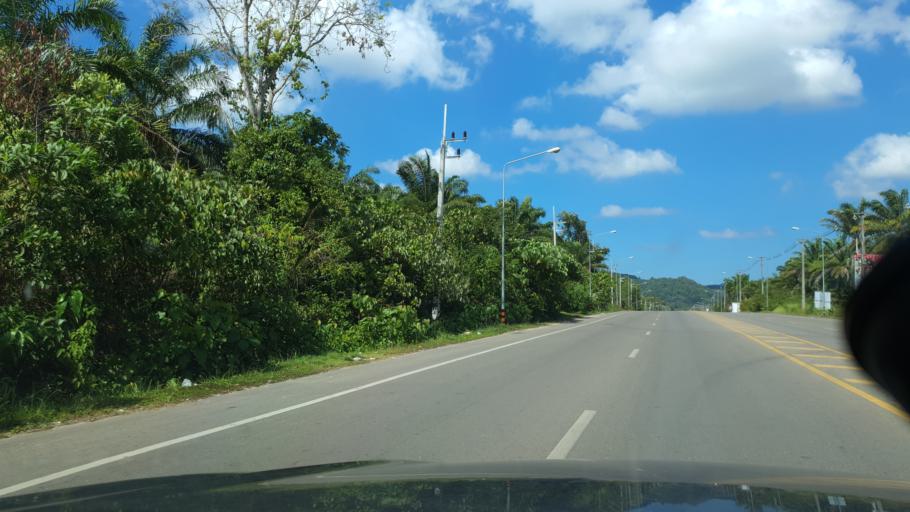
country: TH
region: Phangnga
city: Ban Ao Nang
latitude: 8.0371
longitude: 98.8547
